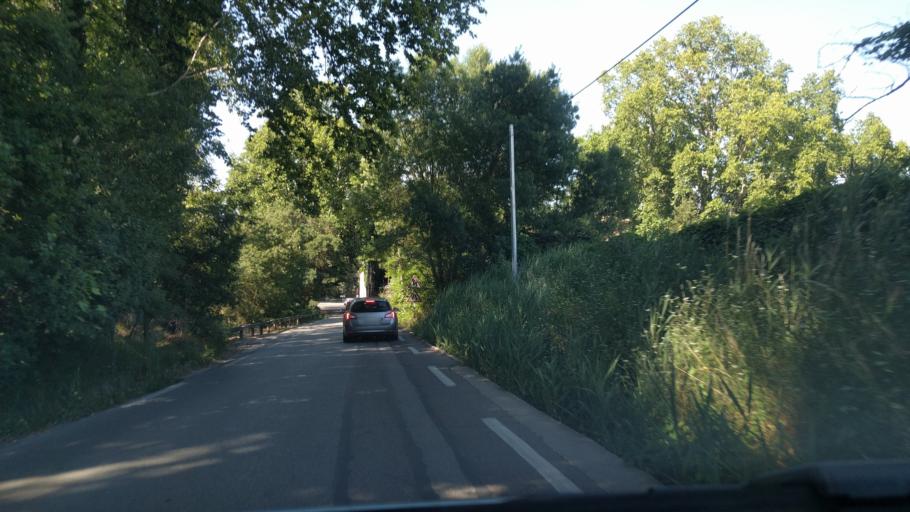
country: FR
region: Provence-Alpes-Cote d'Azur
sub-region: Departement des Bouches-du-Rhone
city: Ventabren
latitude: 43.5043
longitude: 5.3479
